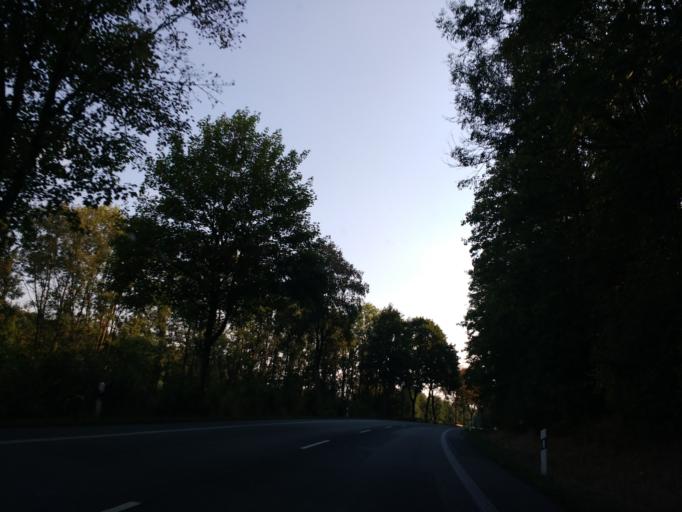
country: DE
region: North Rhine-Westphalia
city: Brakel
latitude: 51.6429
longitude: 9.1376
